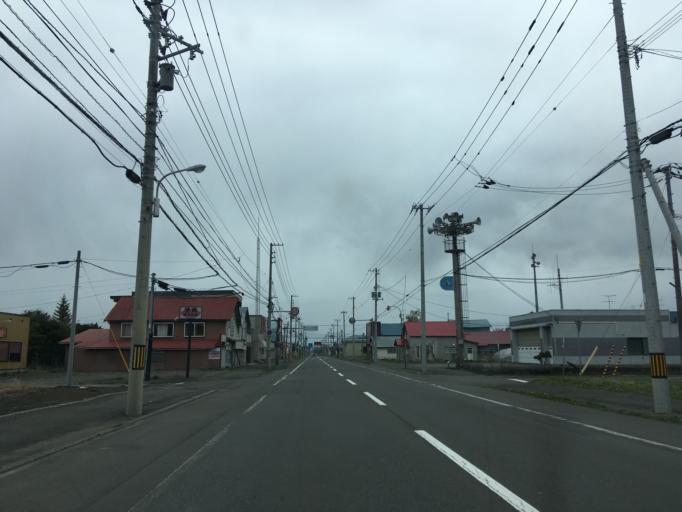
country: JP
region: Hokkaido
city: Chitose
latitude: 42.9438
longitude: 141.8039
